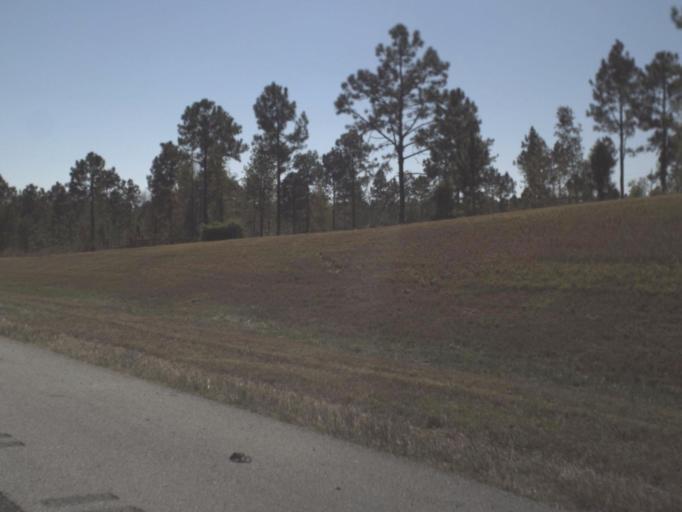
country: US
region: Florida
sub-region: Lake County
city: Minneola
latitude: 28.5946
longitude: -81.7155
